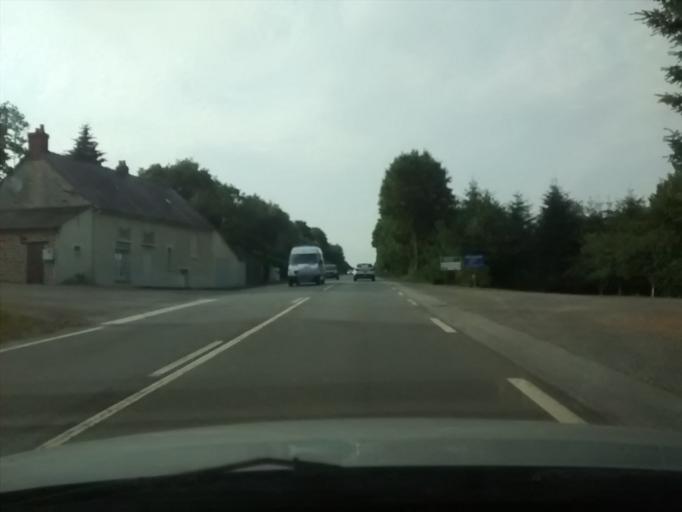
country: FR
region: Brittany
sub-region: Departement d'Ille-et-Vilaine
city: Vitre
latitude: 48.0956
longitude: -1.2059
